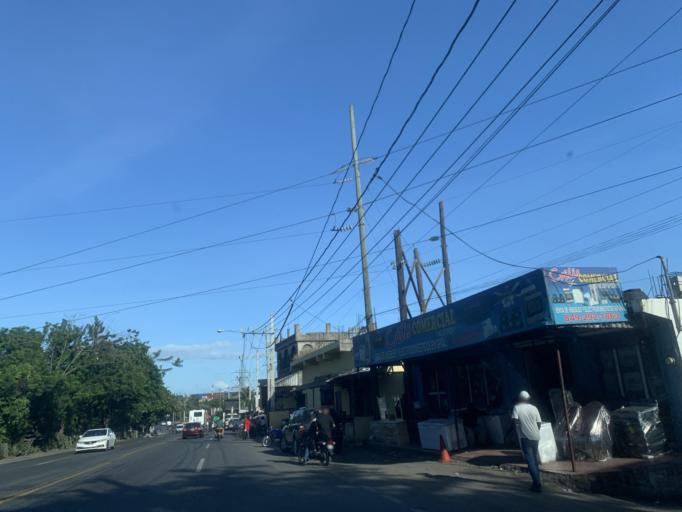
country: DO
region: San Cristobal
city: El Carril
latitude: 18.4336
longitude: -70.0103
